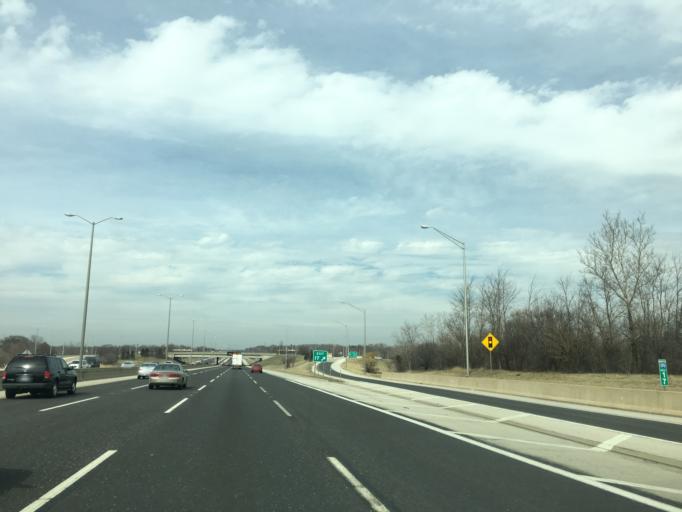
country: US
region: Illinois
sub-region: DuPage County
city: Woodridge
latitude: 41.7690
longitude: -88.0423
